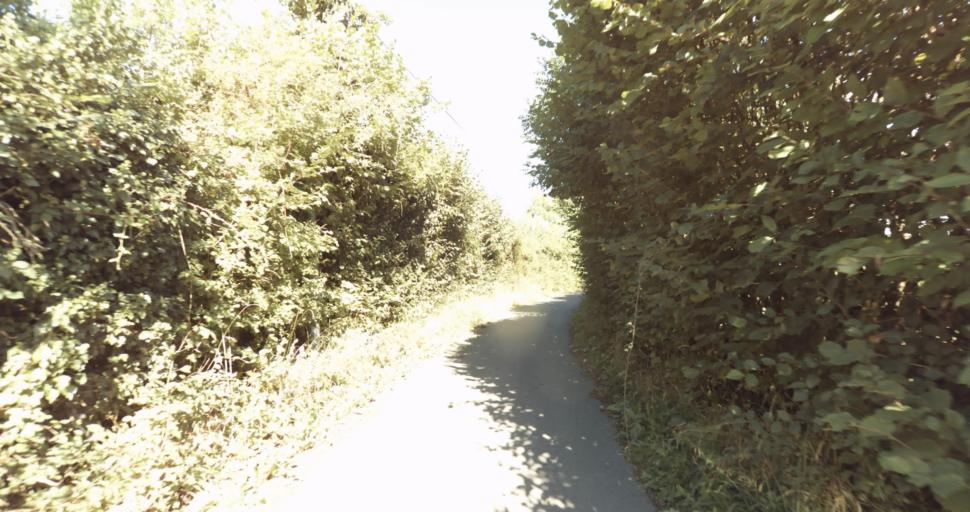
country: FR
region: Lower Normandy
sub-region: Departement de l'Orne
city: Gace
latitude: 48.7995
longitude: 0.2148
